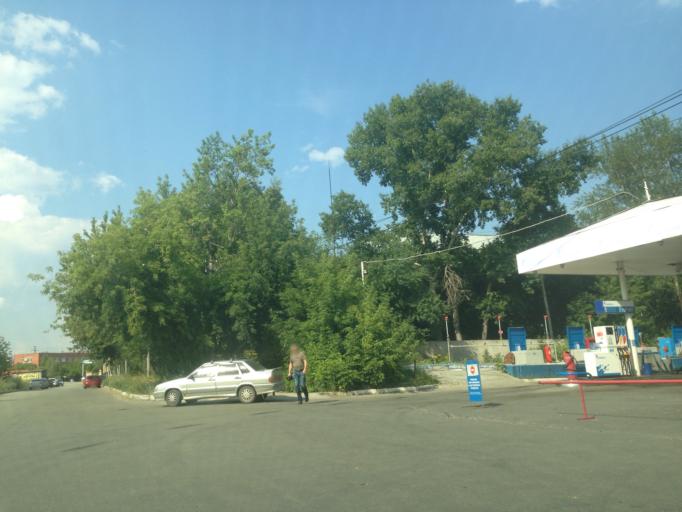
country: RU
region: Sverdlovsk
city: Yekaterinburg
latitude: 56.8668
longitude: 60.6374
